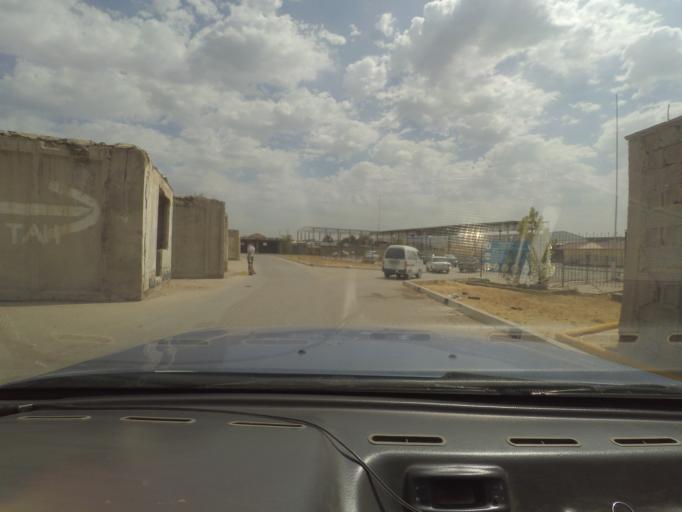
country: UZ
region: Toshkent
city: Urtaowul
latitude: 41.2341
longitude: 69.1541
